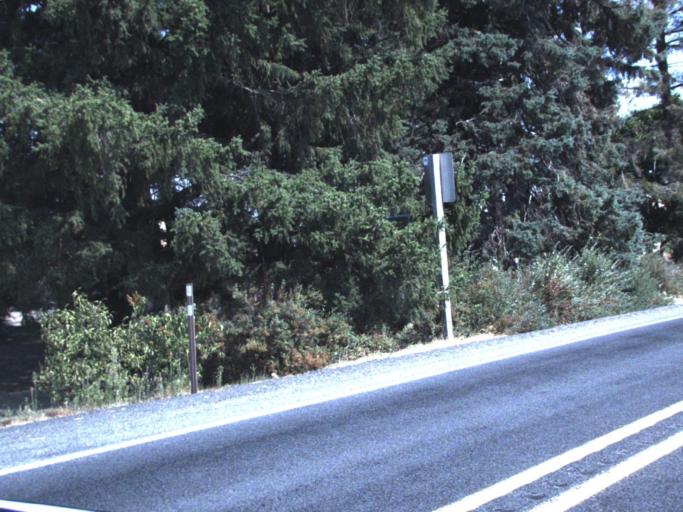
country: US
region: Idaho
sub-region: Benewah County
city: Plummer
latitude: 47.1957
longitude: -117.0991
